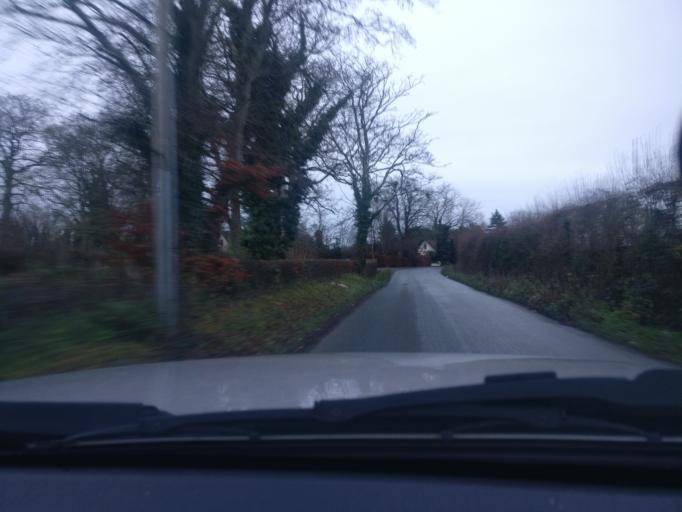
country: IE
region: Leinster
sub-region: Kildare
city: Maynooth
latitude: 53.4127
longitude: -6.6042
